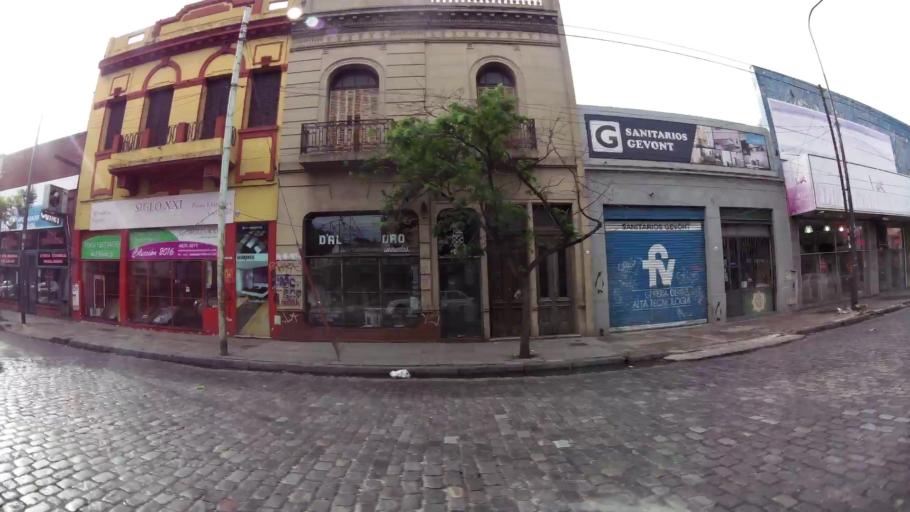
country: AR
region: Buenos Aires F.D.
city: Villa Santa Rita
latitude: -34.6376
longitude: -58.4798
